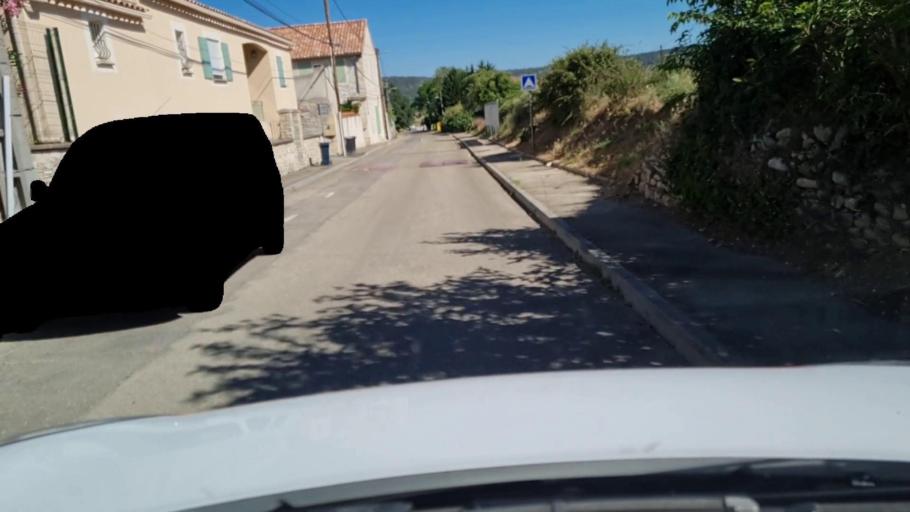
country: FR
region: Languedoc-Roussillon
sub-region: Departement du Gard
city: Nages-et-Solorgues
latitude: 43.8058
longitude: 4.2280
